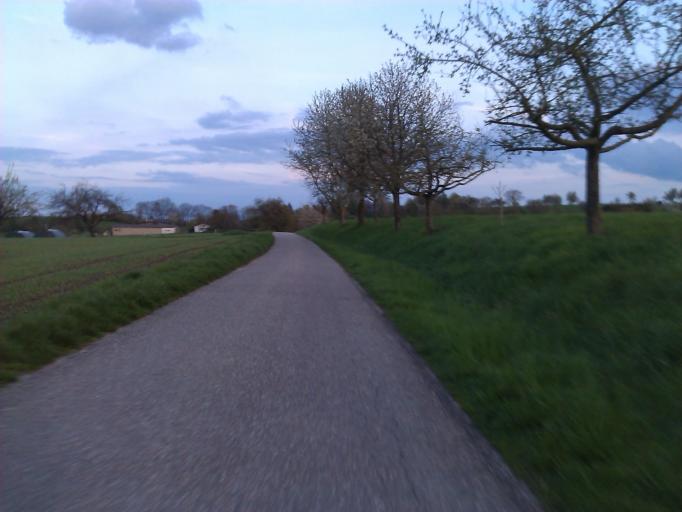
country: DE
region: Baden-Wuerttemberg
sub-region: Regierungsbezirk Stuttgart
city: Bad Wimpfen
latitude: 49.2238
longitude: 9.1698
